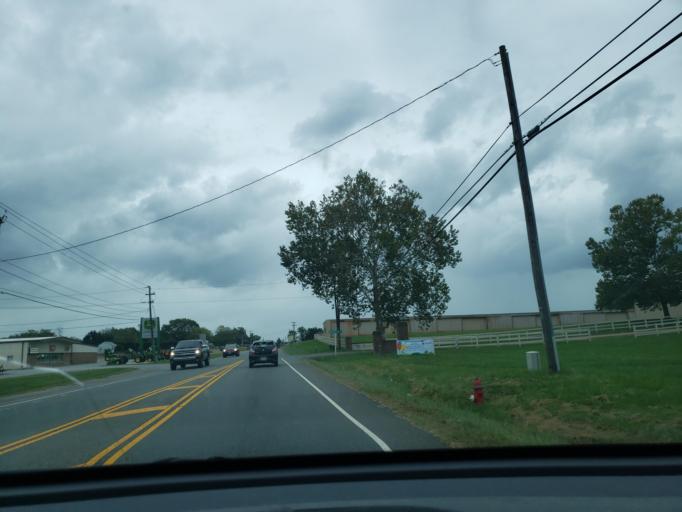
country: US
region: Virginia
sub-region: City of Fredericksburg
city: Fredericksburg
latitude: 38.2709
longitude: -77.4463
